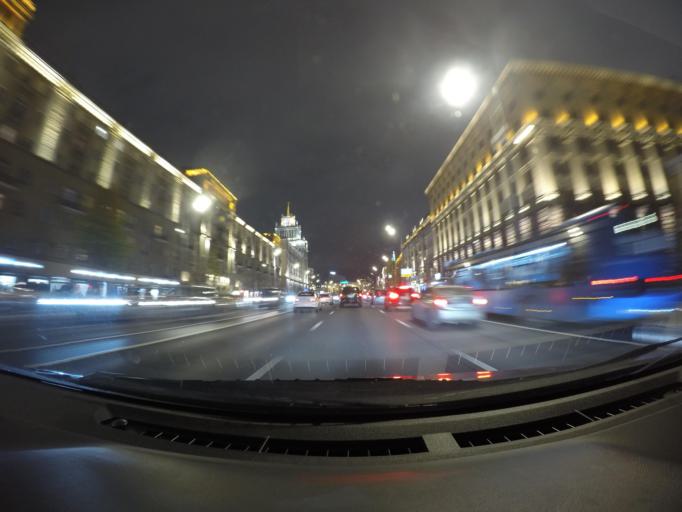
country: RU
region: Moscow
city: Moscow
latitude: 55.7666
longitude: 37.5919
